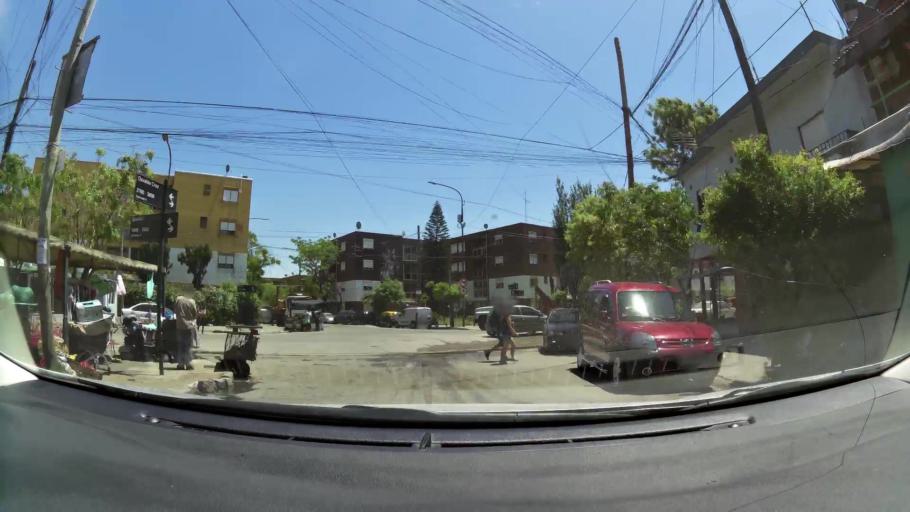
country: AR
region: Buenos Aires
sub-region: Partido de Avellaneda
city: Avellaneda
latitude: -34.6560
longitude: -58.4026
